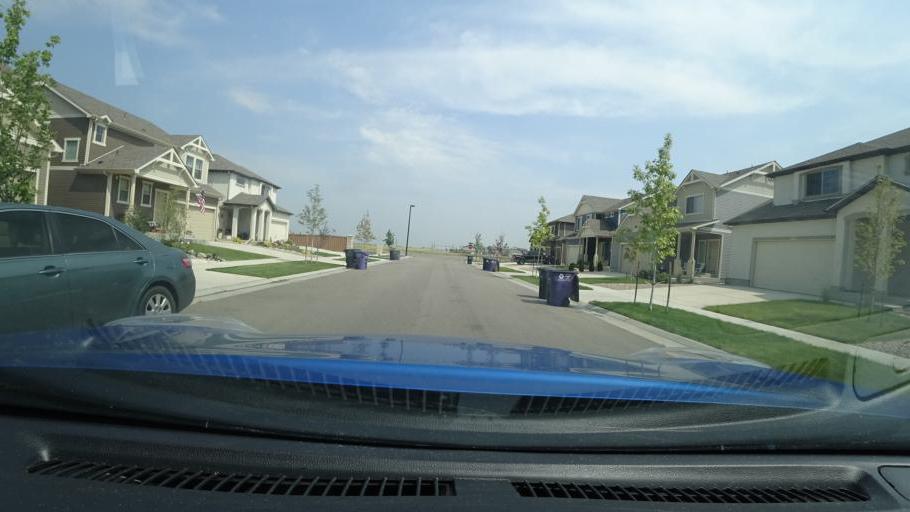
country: US
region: Colorado
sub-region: Adams County
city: Aurora
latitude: 39.7786
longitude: -104.7820
